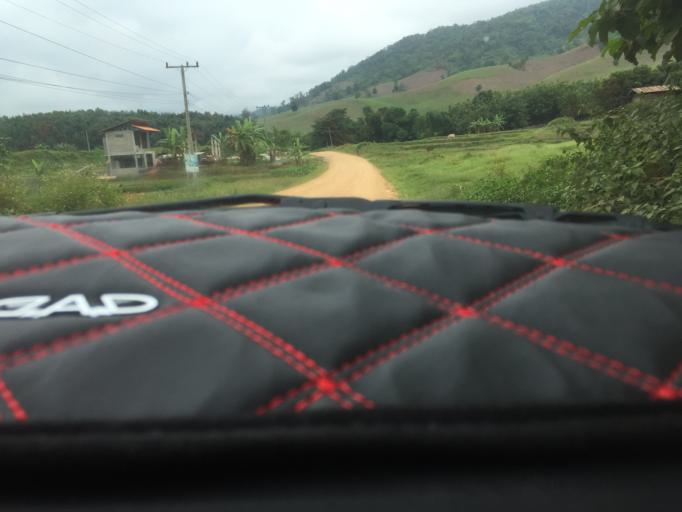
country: TH
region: Phayao
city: Phu Sang
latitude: 19.6926
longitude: 100.5015
